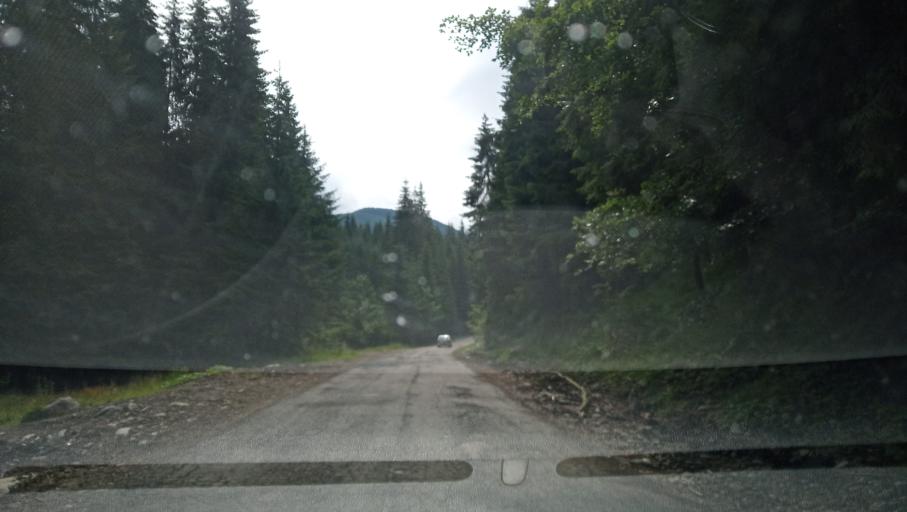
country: RO
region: Hunedoara
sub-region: Oras Petrila
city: Petrila
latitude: 45.4095
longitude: 23.5554
